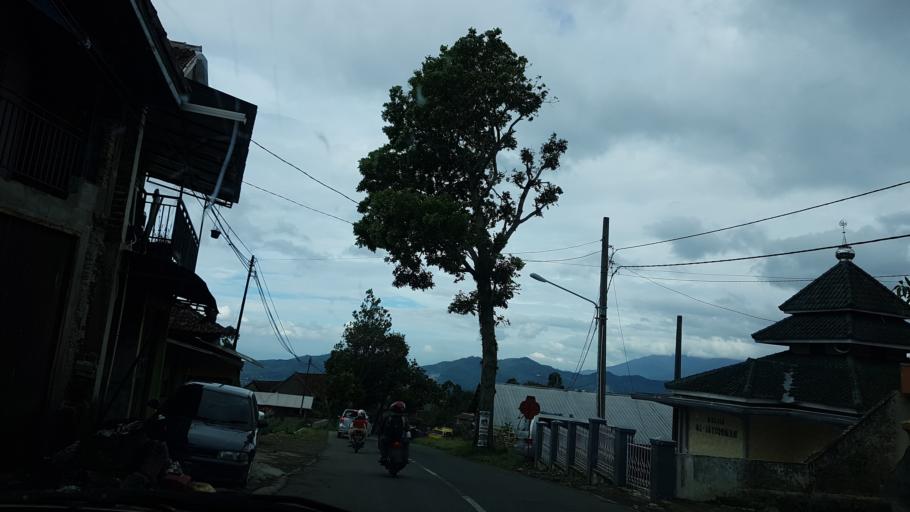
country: ID
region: West Java
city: Banjar
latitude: -7.1220
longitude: 107.4290
